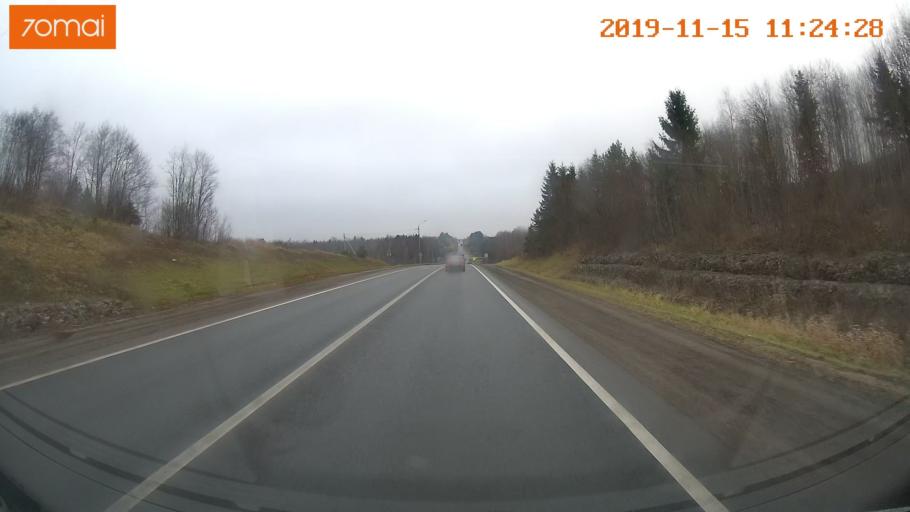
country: RU
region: Vologda
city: Molochnoye
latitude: 59.1573
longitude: 39.4057
